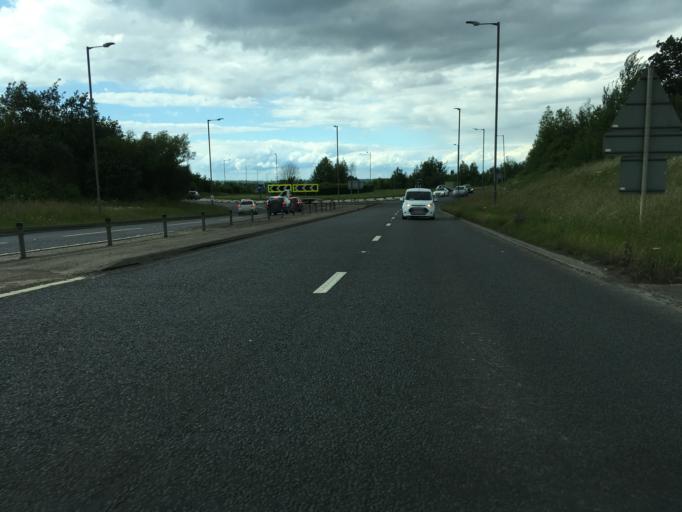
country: GB
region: England
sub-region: Central Bedfordshire
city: Leighton Buzzard
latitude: 51.9337
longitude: -0.6969
